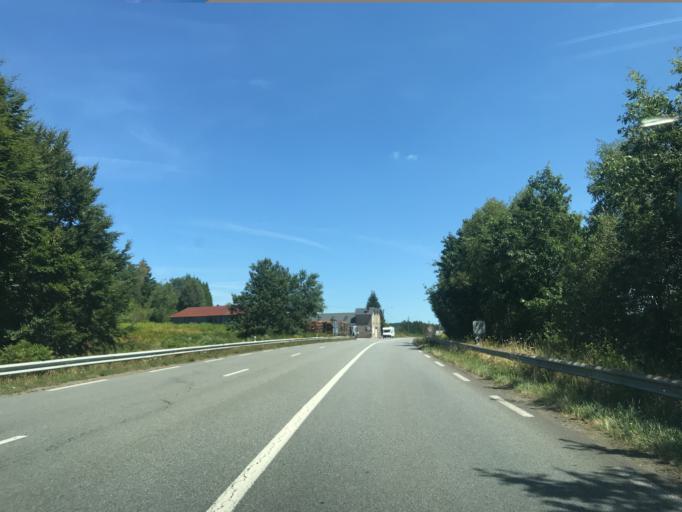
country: FR
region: Limousin
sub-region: Departement de la Correze
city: Correze
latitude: 45.3395
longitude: 1.9262
